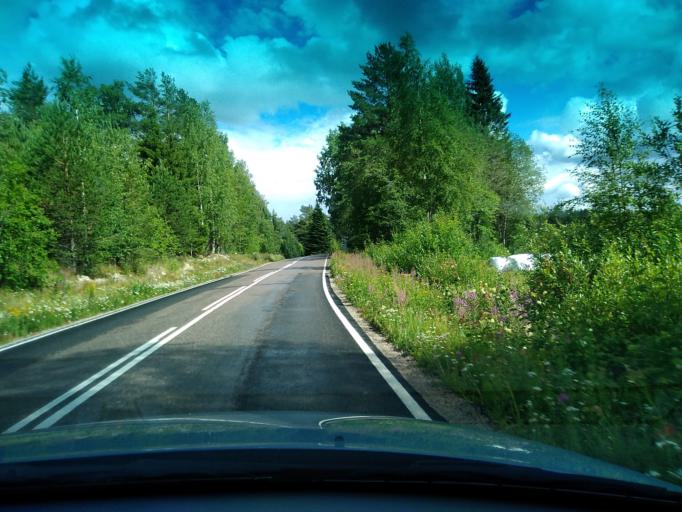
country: FI
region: Central Finland
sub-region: Saarijaervi-Viitasaari
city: Saarijaervi
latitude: 62.7349
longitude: 25.1359
